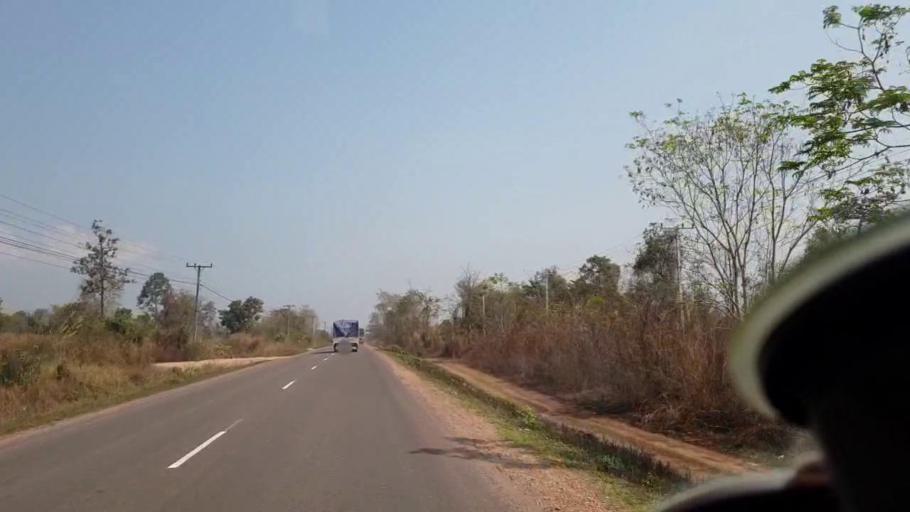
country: TH
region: Nong Khai
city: Phon Phisai
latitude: 18.0991
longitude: 103.0182
